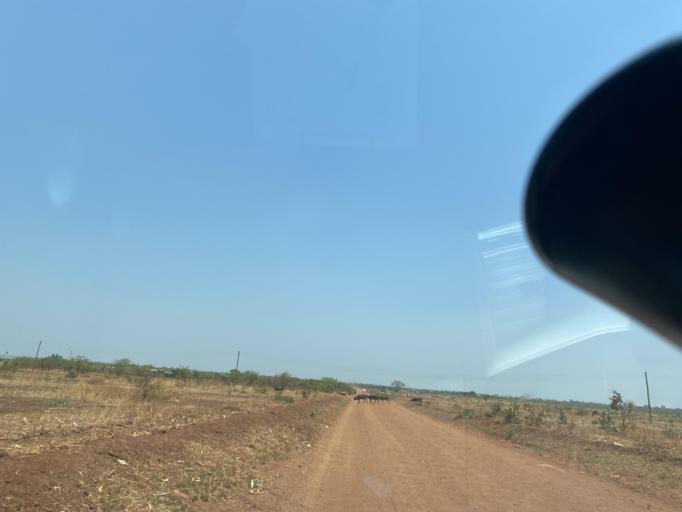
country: ZM
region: Southern
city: Nakambala
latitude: -15.5032
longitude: 27.9246
